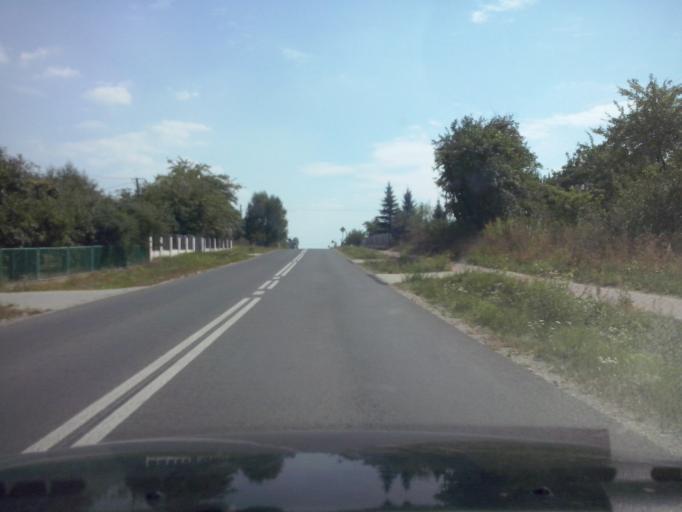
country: PL
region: Swietokrzyskie
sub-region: Powiat buski
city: Gnojno
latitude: 50.6057
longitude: 20.8364
